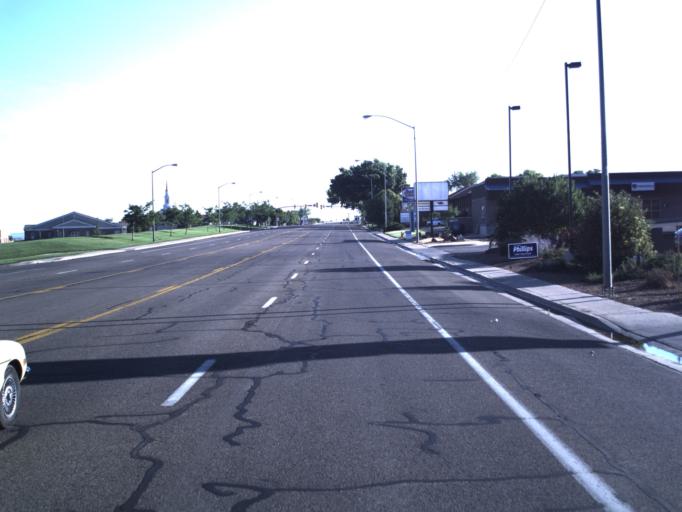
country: US
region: Utah
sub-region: Iron County
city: Cedar City
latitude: 37.7095
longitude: -113.0617
